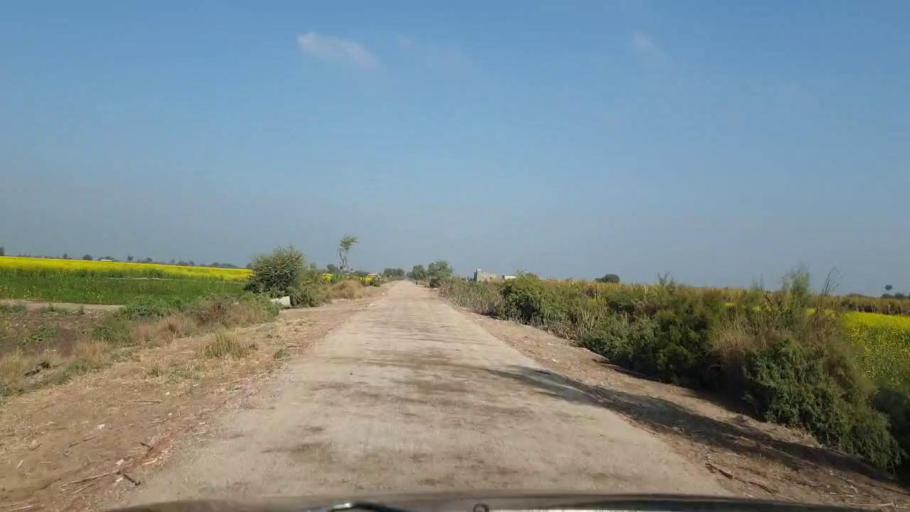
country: PK
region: Sindh
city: Sinjhoro
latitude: 26.0561
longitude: 68.7728
